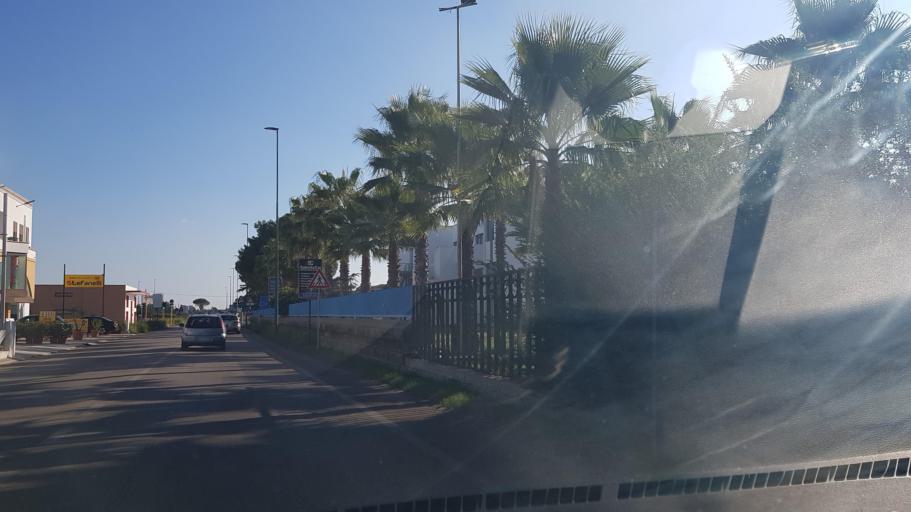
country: IT
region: Apulia
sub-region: Provincia di Lecce
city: Montesano Salentino
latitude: 39.9756
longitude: 18.3254
